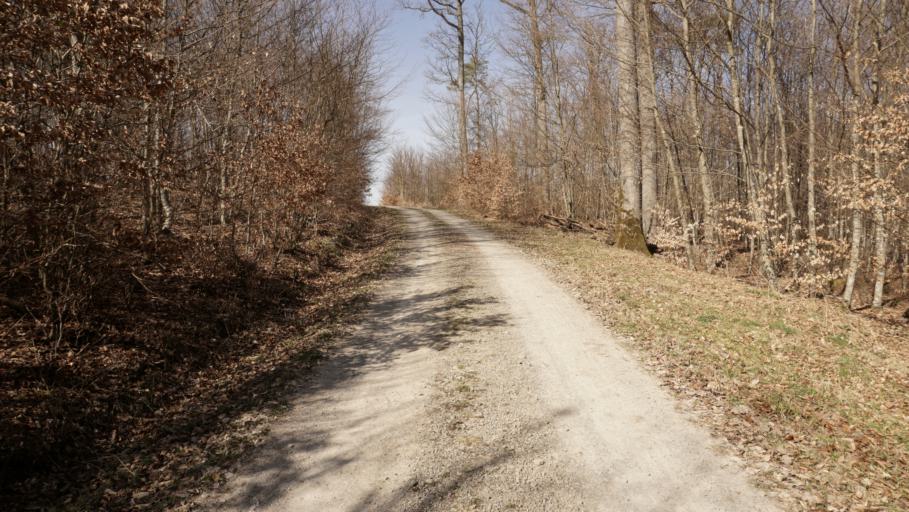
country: DE
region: Baden-Wuerttemberg
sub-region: Karlsruhe Region
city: Mosbach
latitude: 49.3826
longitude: 9.1429
